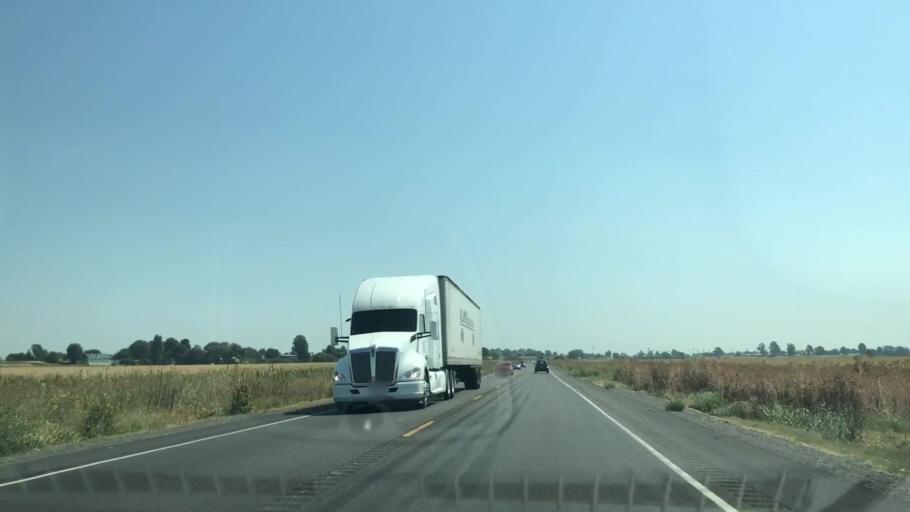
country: US
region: California
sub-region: Solano County
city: Rio Vista
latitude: 38.1341
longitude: -121.6024
